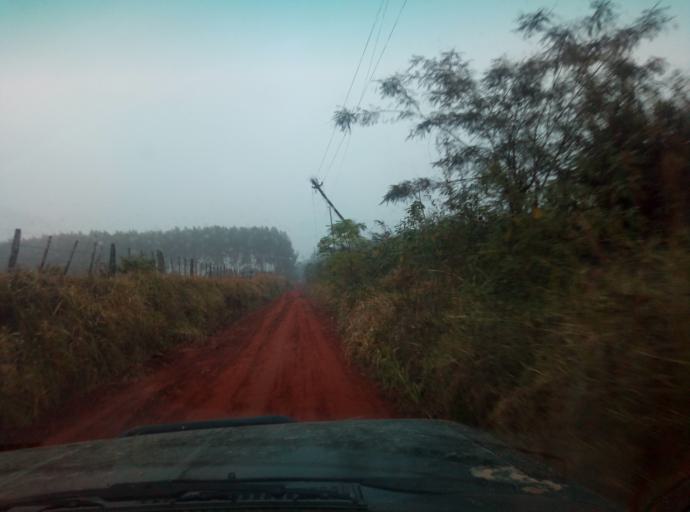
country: PY
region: Caaguazu
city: Doctor Cecilio Baez
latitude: -25.1617
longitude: -56.2620
